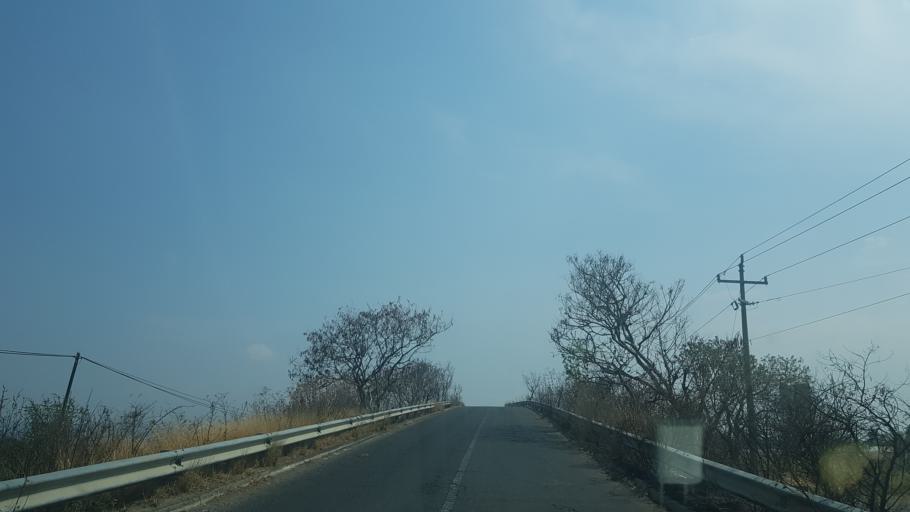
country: MX
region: Puebla
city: San Juan Tianguismanalco
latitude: 18.9360
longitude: -98.4542
